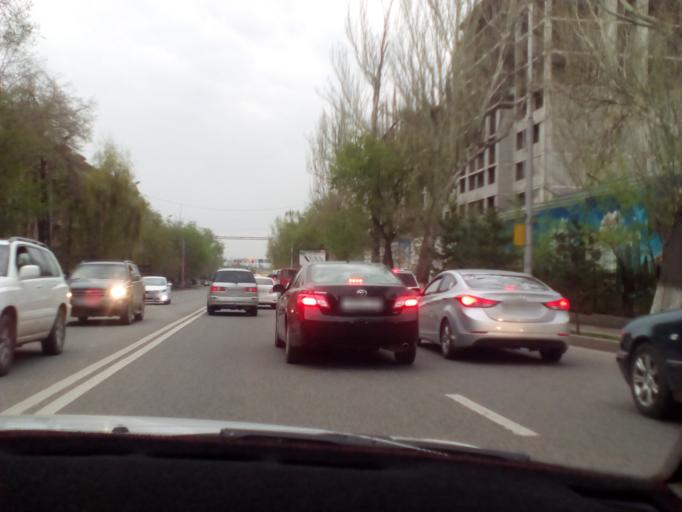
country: KZ
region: Almaty Qalasy
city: Almaty
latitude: 43.2678
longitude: 76.9451
